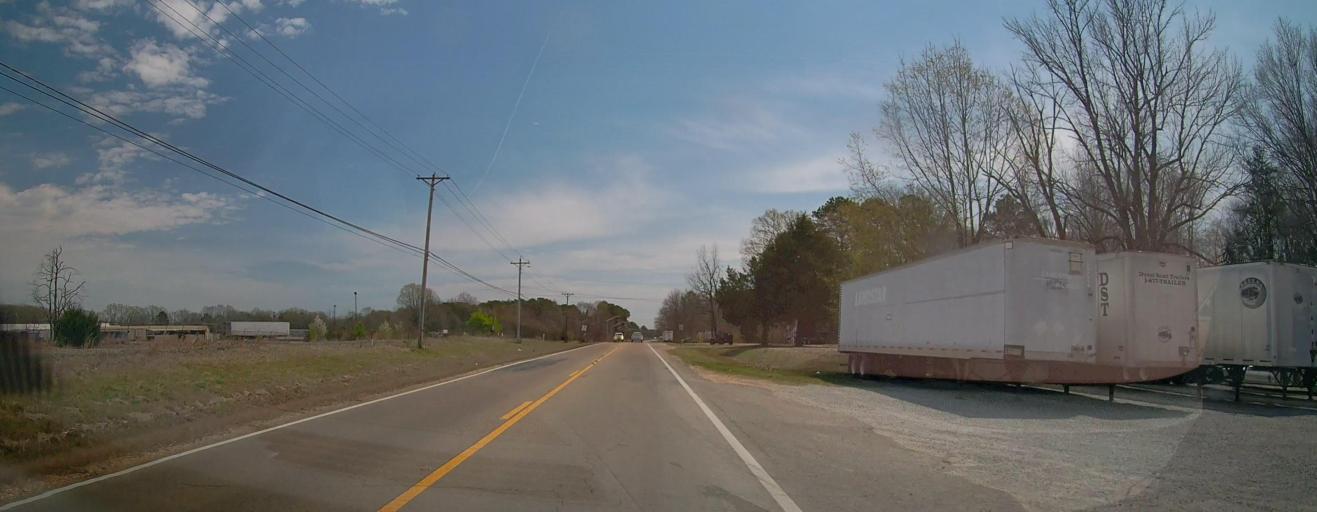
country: US
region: Mississippi
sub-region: Union County
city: New Albany
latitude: 34.5161
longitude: -89.0461
